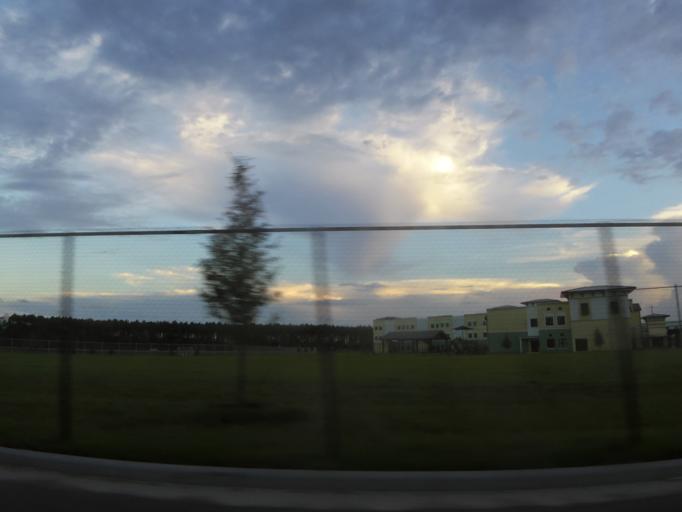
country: US
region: Florida
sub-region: Saint Johns County
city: Palm Valley
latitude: 30.1223
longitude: -81.4071
